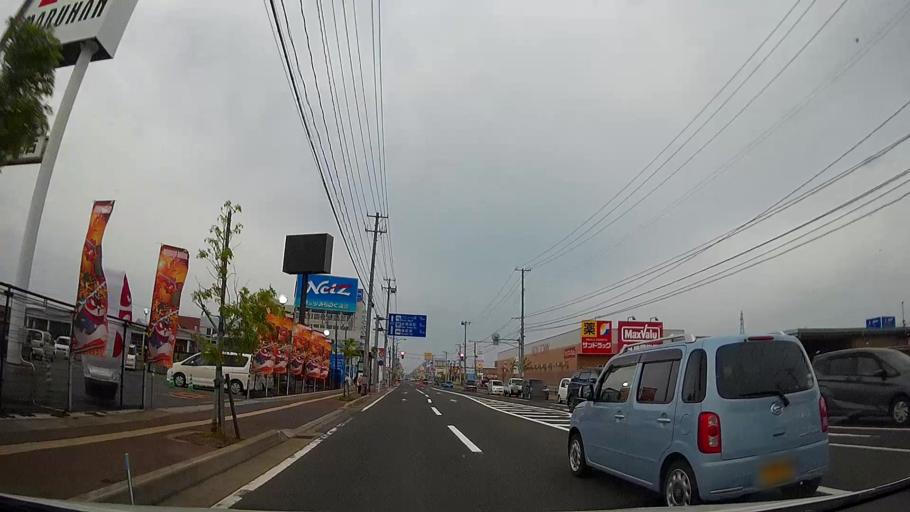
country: JP
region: Aomori
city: Aomori Shi
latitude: 40.7974
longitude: 140.7582
